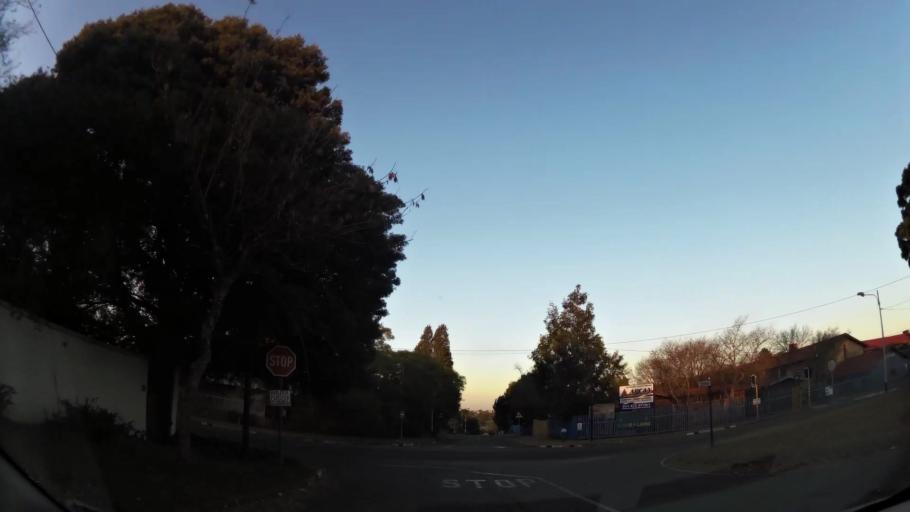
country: ZA
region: Gauteng
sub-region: City of Johannesburg Metropolitan Municipality
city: Roodepoort
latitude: -26.1612
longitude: 27.8997
